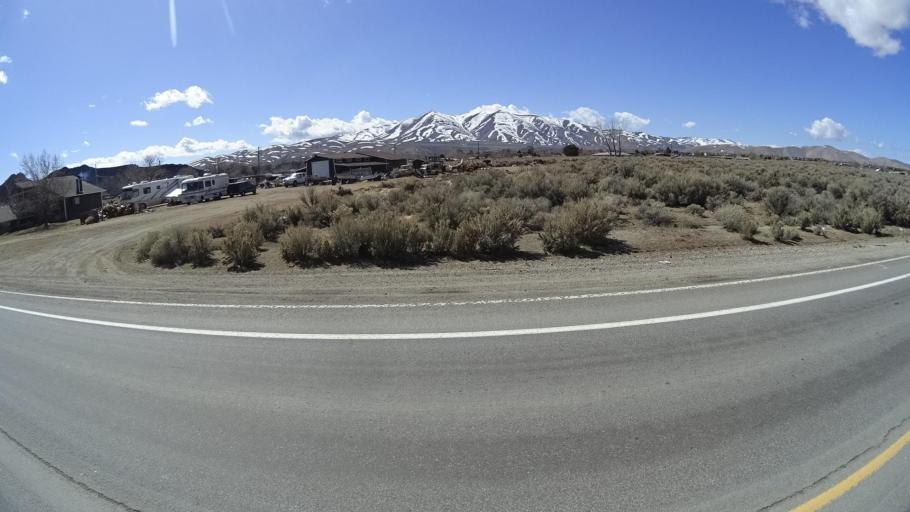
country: US
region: Nevada
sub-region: Washoe County
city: Lemmon Valley
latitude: 39.6342
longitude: -119.8555
